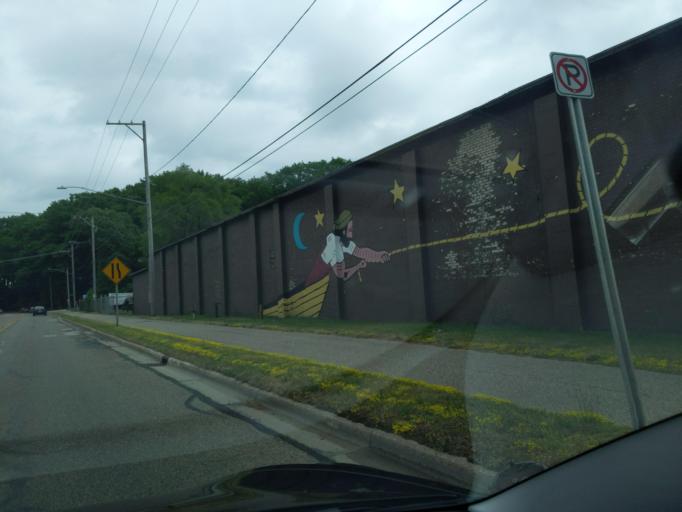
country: US
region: Michigan
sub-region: Muskegon County
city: Roosevelt Park
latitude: 43.2150
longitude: -86.3175
